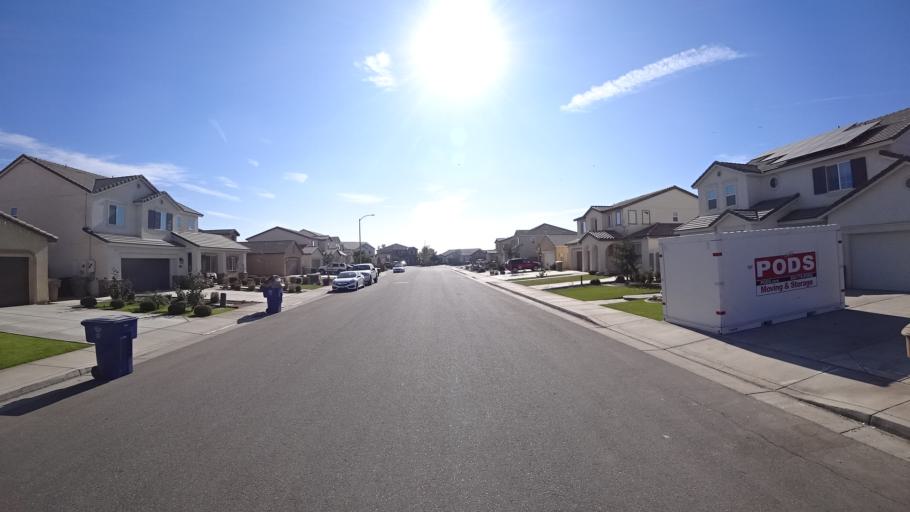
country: US
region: California
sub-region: Kern County
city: Greenfield
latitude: 35.2834
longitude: -119.0578
